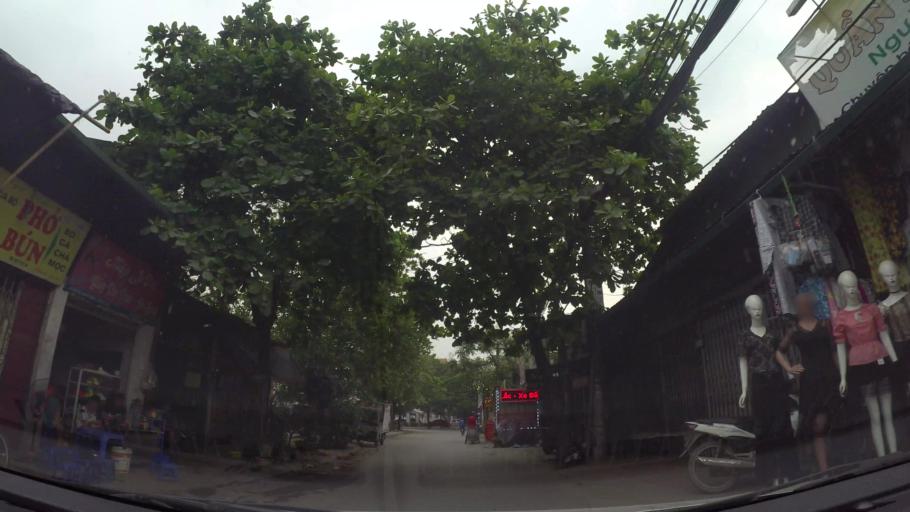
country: VN
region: Ha Noi
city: Cau Dien
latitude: 21.0343
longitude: 105.7440
